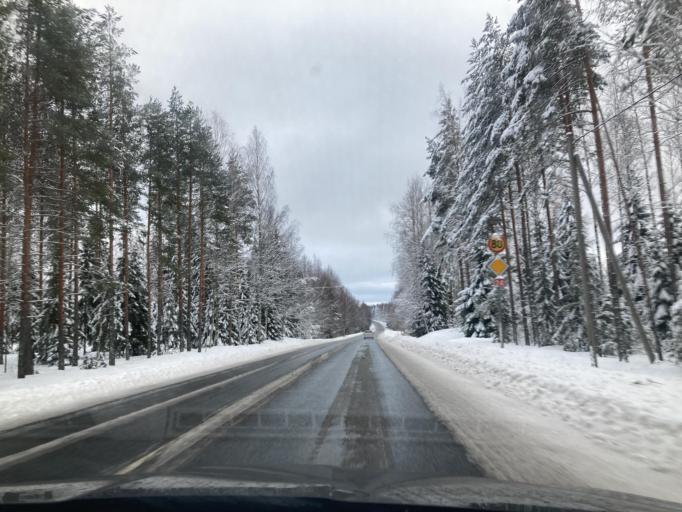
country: FI
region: Paijanne Tavastia
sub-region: Lahti
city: Padasjoki
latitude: 61.3029
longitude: 25.2978
